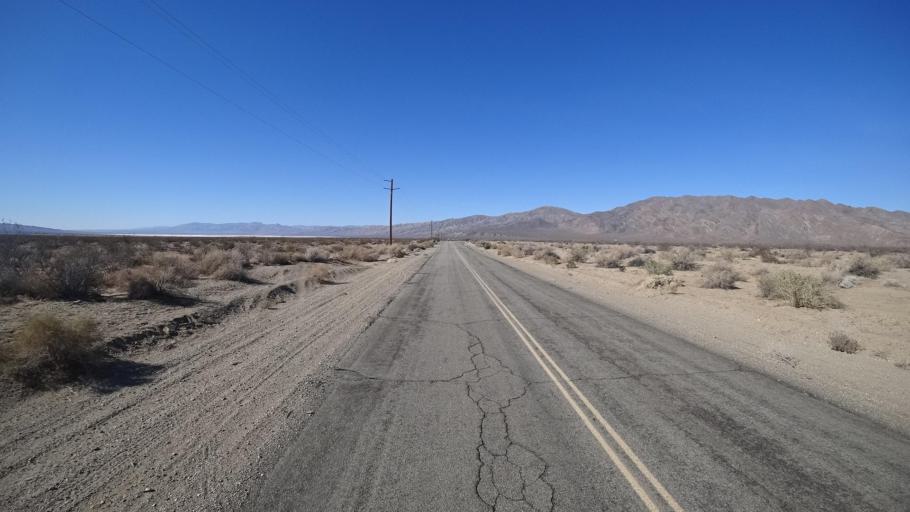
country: US
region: California
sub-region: Kern County
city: Ridgecrest
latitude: 35.3883
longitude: -117.7577
